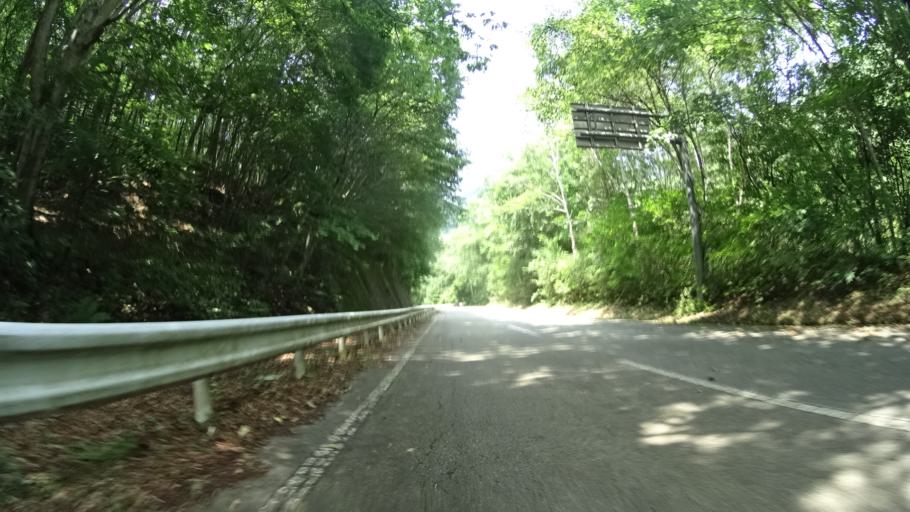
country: JP
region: Nagano
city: Saku
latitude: 36.1203
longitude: 138.6092
